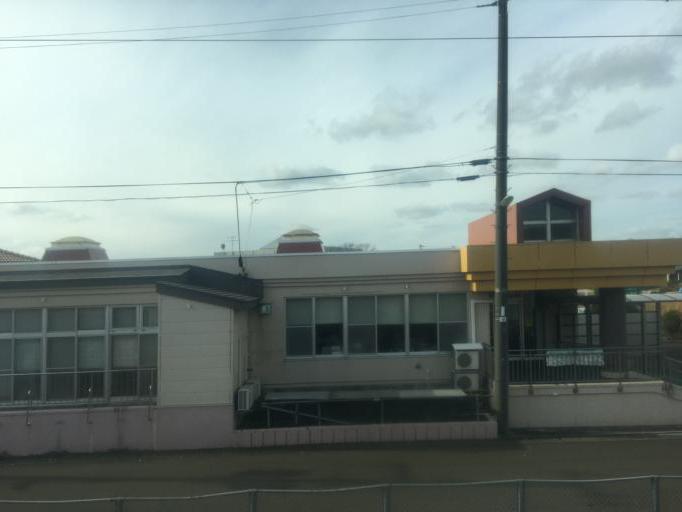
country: JP
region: Akita
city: Tenno
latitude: 39.9428
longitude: 140.0798
